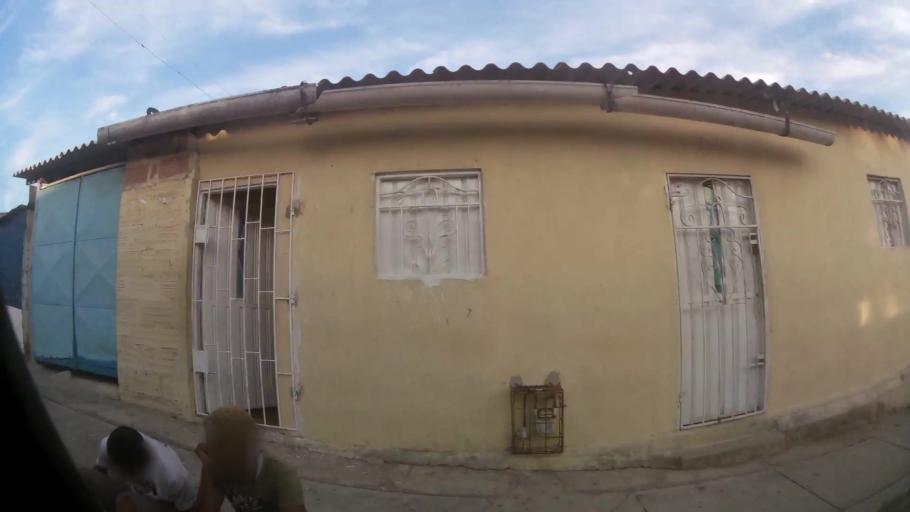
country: CO
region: Atlantico
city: Barranquilla
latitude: 10.9588
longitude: -74.8216
